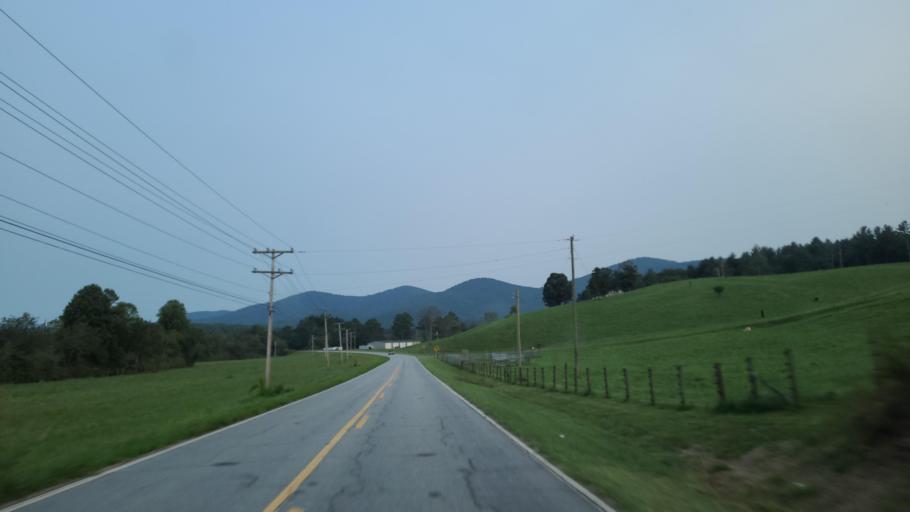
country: US
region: Georgia
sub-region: Union County
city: Blairsville
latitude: 34.8397
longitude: -84.0882
